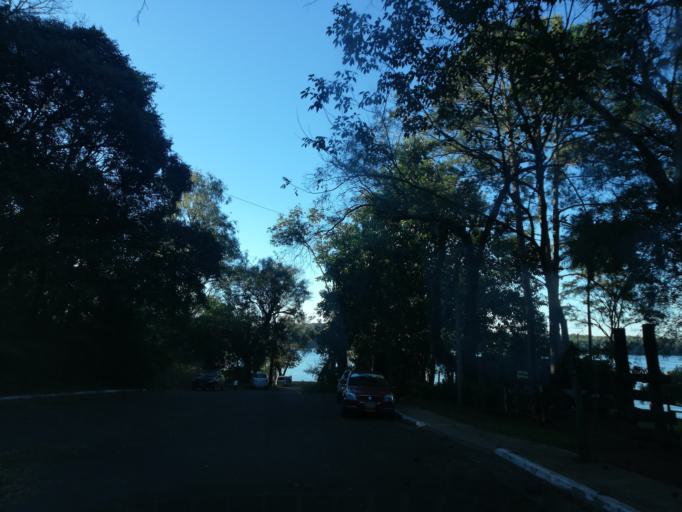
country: AR
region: Misiones
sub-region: Departamento de Candelaria
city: Candelaria
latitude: -27.4492
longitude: -55.7469
